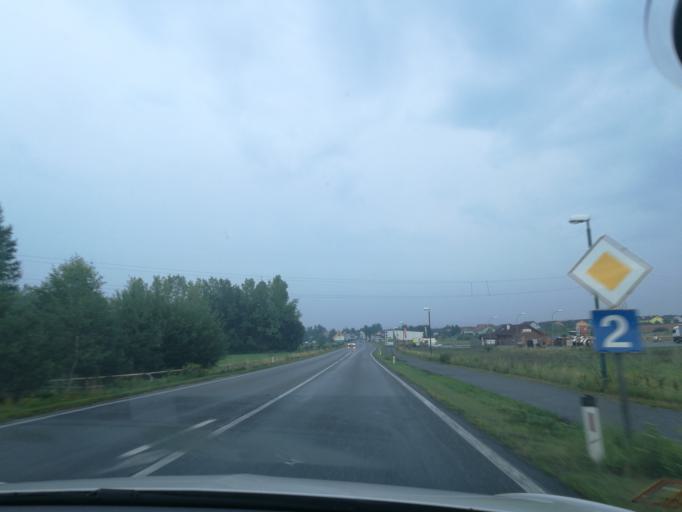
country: AT
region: Lower Austria
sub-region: Politischer Bezirk Zwettl
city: Gopfritz an der Wild
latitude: 48.7290
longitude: 15.3910
